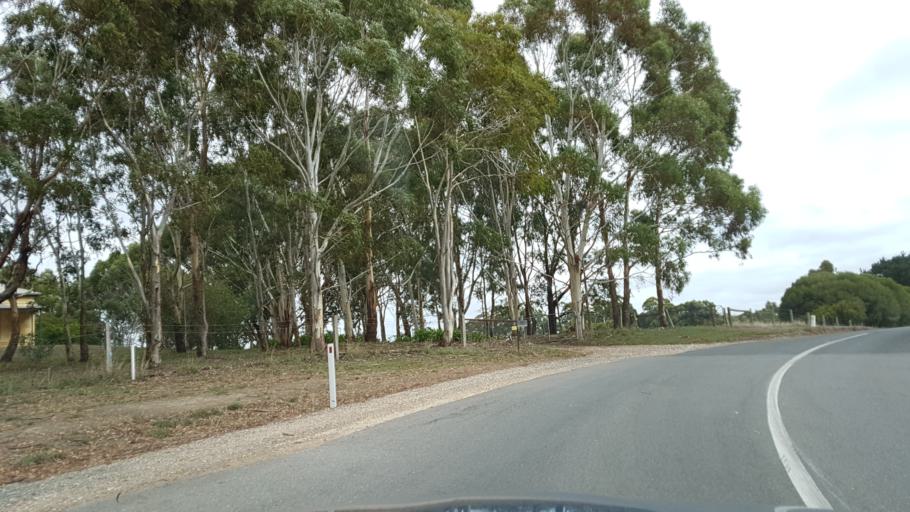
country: AU
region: South Australia
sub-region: Mount Barker
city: Little Hampton
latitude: -35.0797
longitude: 138.8197
